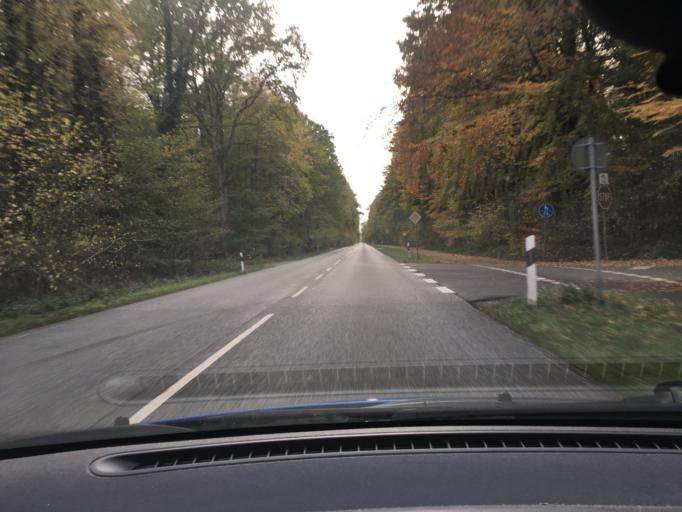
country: DE
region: Schleswig-Holstein
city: Sahms
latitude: 53.5399
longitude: 10.5317
